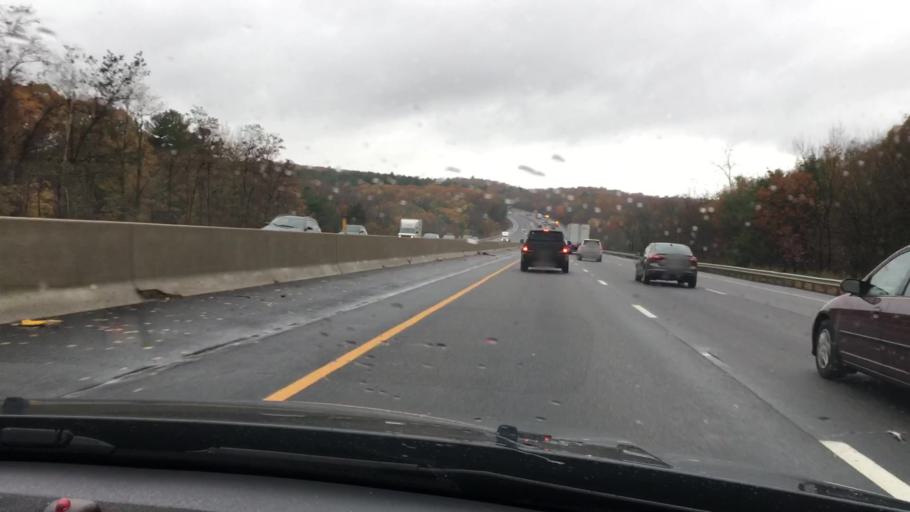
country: US
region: Massachusetts
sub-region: Worcester County
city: Grafton
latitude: 42.2280
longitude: -71.6460
